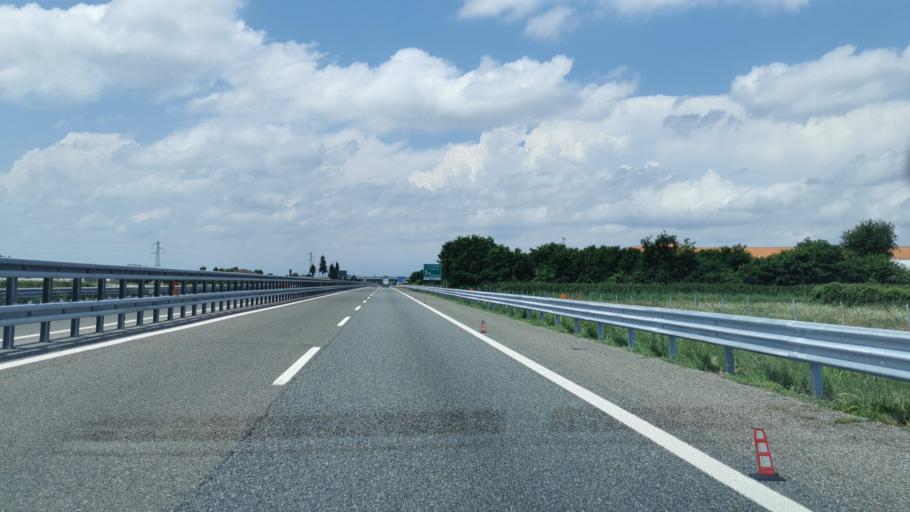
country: IT
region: Piedmont
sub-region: Provincia di Torino
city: Cambiano
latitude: 44.9596
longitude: 7.7985
